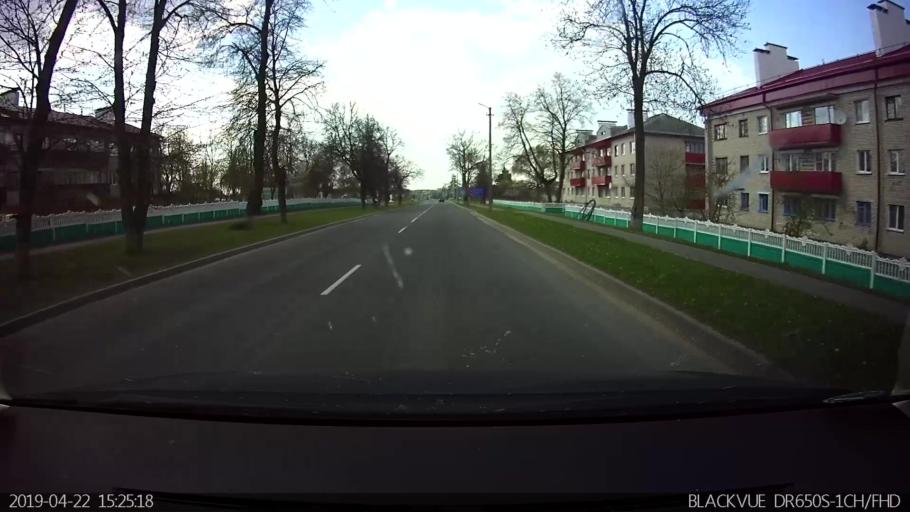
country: BY
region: Brest
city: Vysokaye
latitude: 52.3640
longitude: 23.3974
